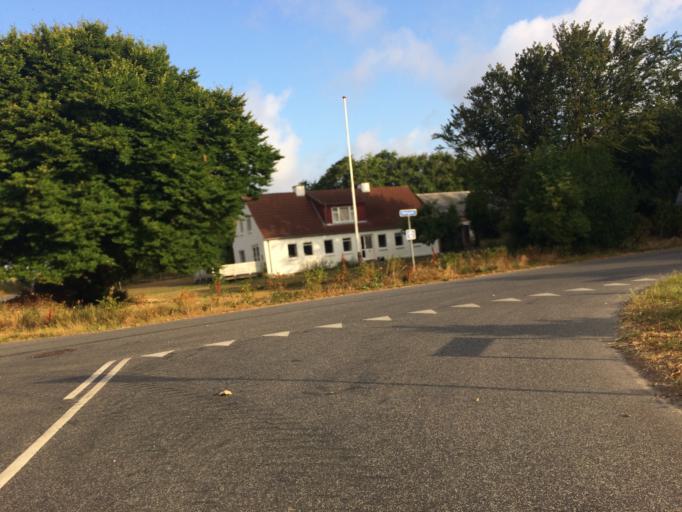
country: DK
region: Central Jutland
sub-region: Holstebro Kommune
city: Vinderup
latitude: 56.5973
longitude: 8.7305
